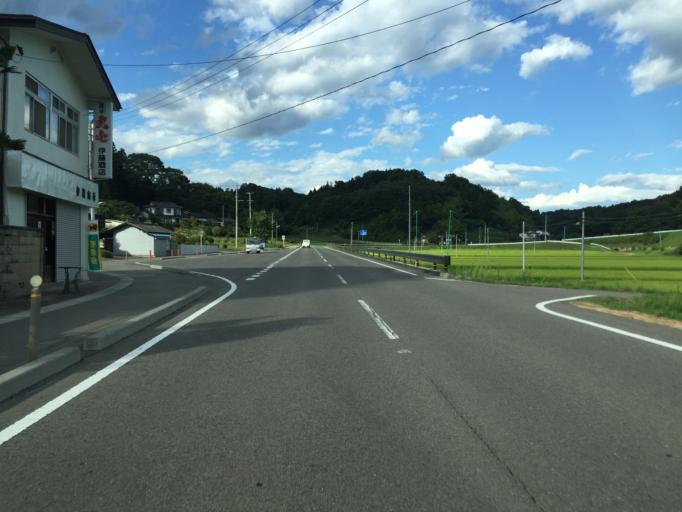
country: JP
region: Fukushima
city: Fukushima-shi
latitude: 37.6734
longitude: 140.5320
